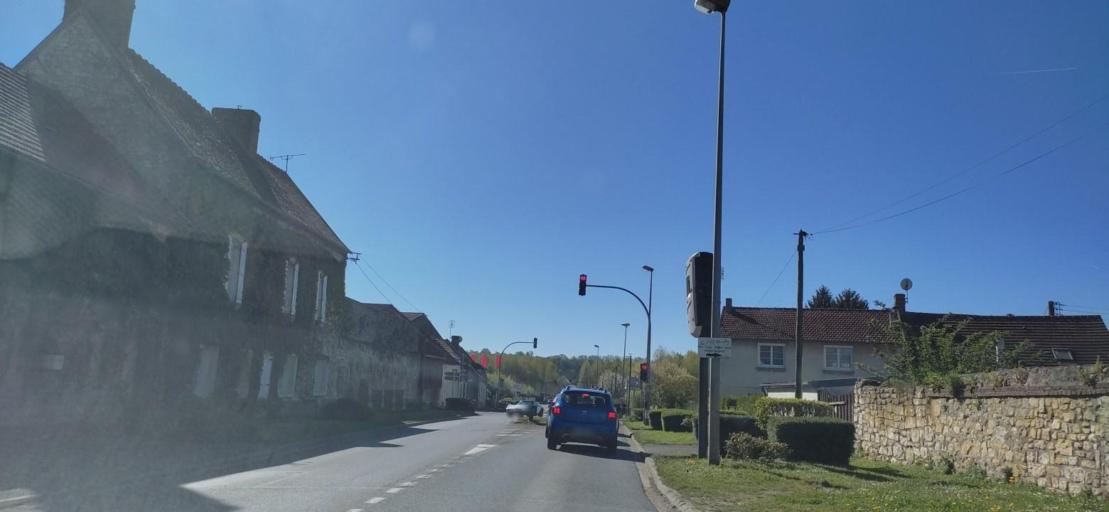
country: FR
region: Picardie
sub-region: Departement de l'Oise
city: Villers-sur-Coudun
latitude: 49.4710
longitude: 2.7561
